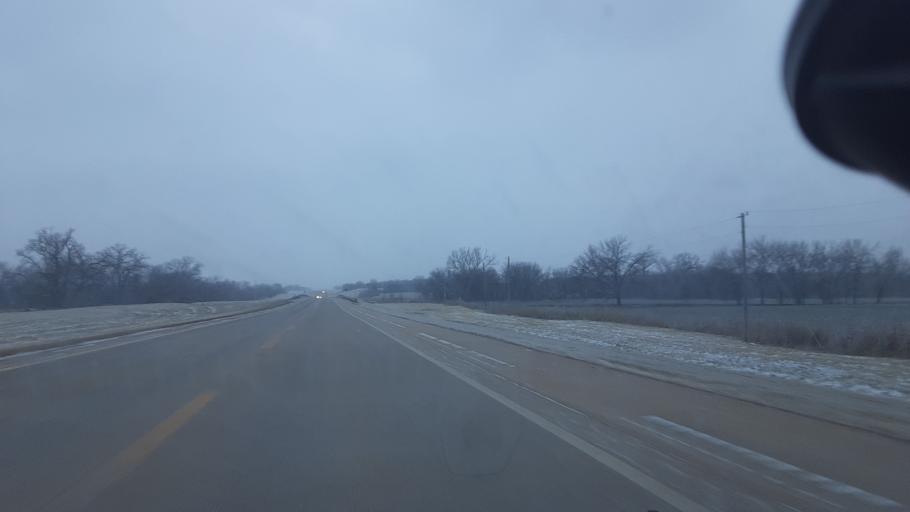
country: US
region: Oklahoma
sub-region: Payne County
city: Perkins
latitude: 35.9859
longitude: -97.1159
